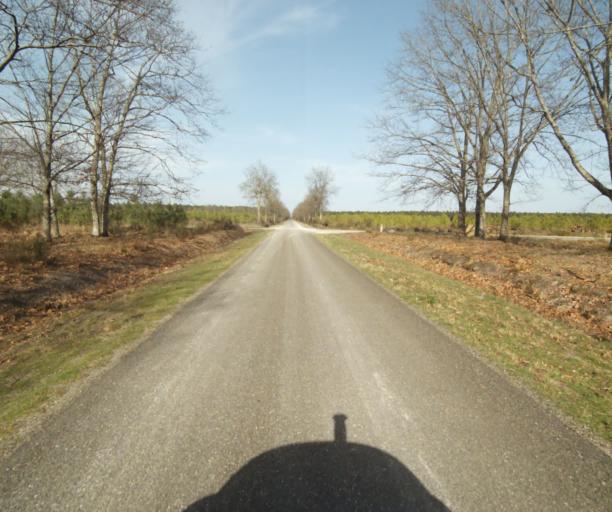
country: FR
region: Aquitaine
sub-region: Departement des Landes
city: Roquefort
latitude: 44.1648
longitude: -0.1652
